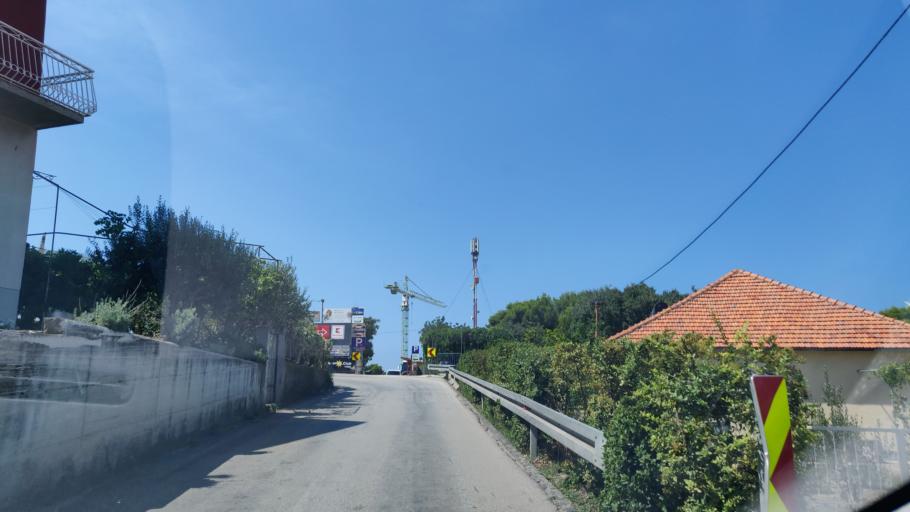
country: HR
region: Splitsko-Dalmatinska
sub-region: Grad Trogir
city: Trogir
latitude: 43.5124
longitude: 16.2483
